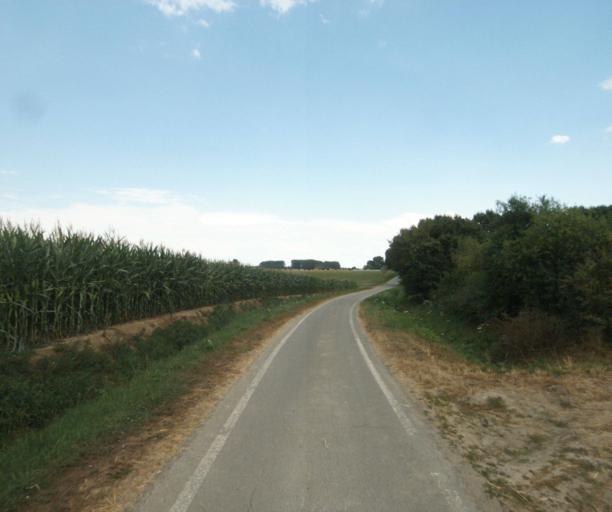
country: FR
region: Nord-Pas-de-Calais
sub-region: Departement du Nord
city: Deulemont
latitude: 50.7250
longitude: 2.9632
